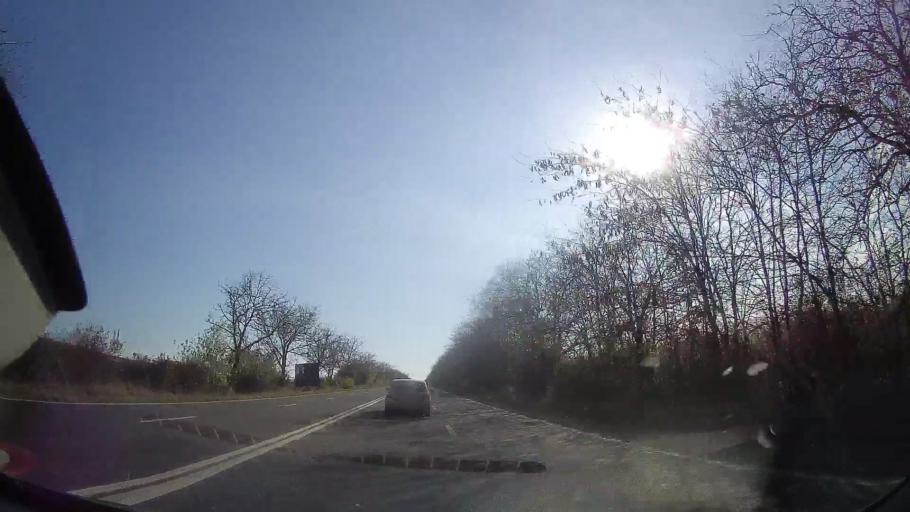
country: RO
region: Constanta
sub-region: Comuna Douazeci si Trei August
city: Douazeci si Trei August
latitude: 43.8950
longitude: 28.5717
